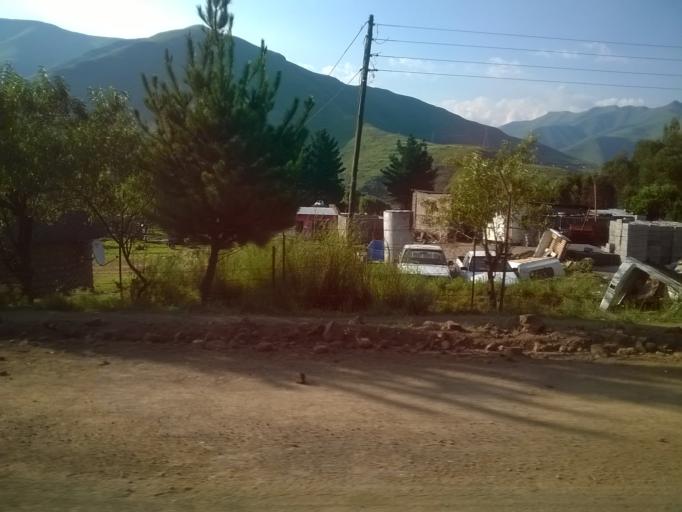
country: LS
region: Butha-Buthe
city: Butha-Buthe
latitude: -29.1076
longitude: 28.4936
